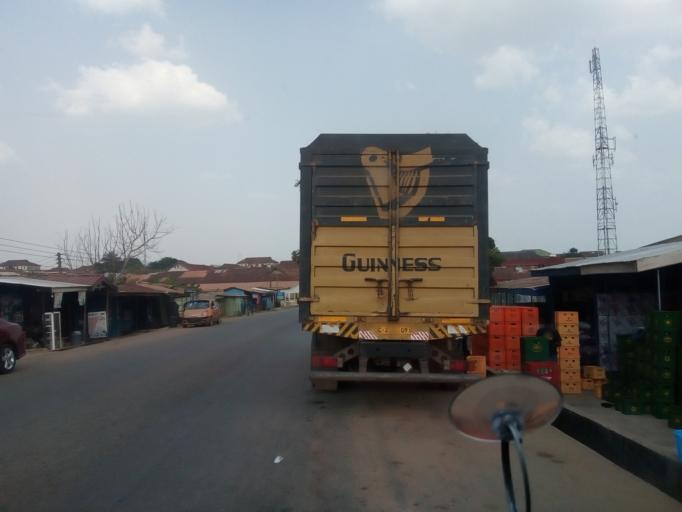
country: GH
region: Eastern
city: Suhum
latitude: 6.0373
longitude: -0.4537
